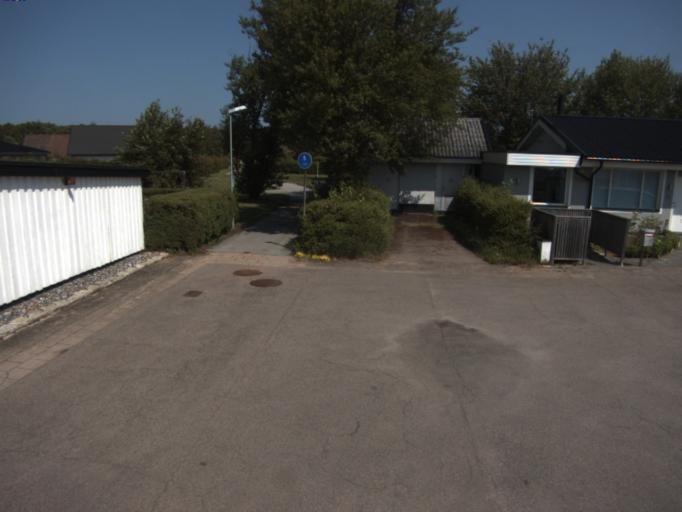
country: SE
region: Skane
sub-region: Helsingborg
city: Helsingborg
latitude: 56.0513
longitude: 12.7383
